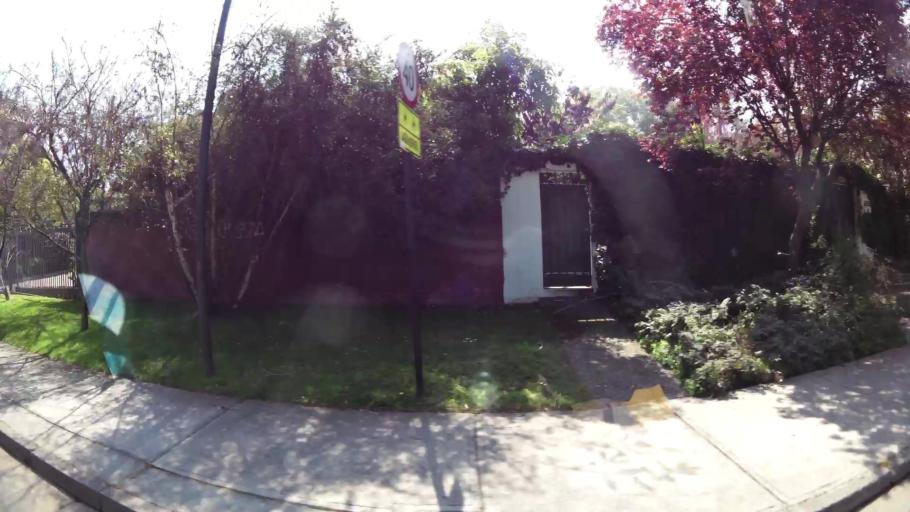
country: CL
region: Santiago Metropolitan
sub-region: Provincia de Santiago
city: Villa Presidente Frei, Nunoa, Santiago, Chile
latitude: -33.3853
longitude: -70.5691
